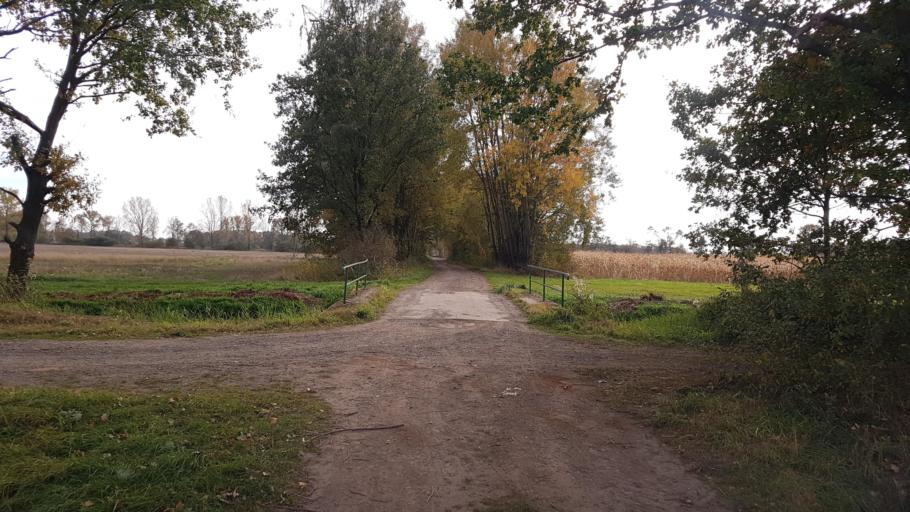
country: DE
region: Brandenburg
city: Schraden
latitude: 51.4510
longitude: 13.6917
